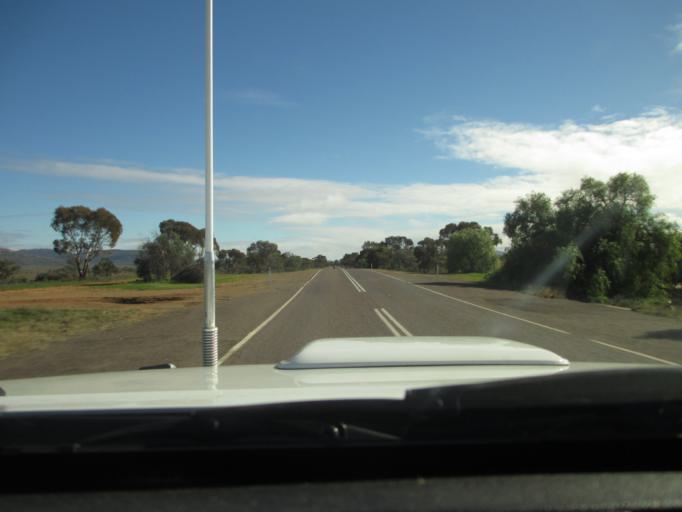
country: AU
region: South Australia
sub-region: Flinders Ranges
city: Quorn
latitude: -31.8995
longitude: 138.4320
